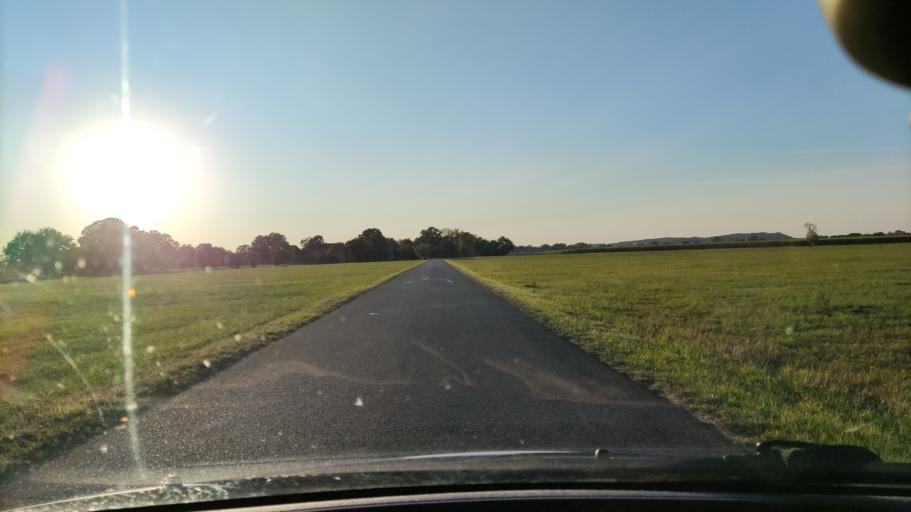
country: DE
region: Lower Saxony
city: Dannenberg
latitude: 53.1280
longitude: 11.0915
